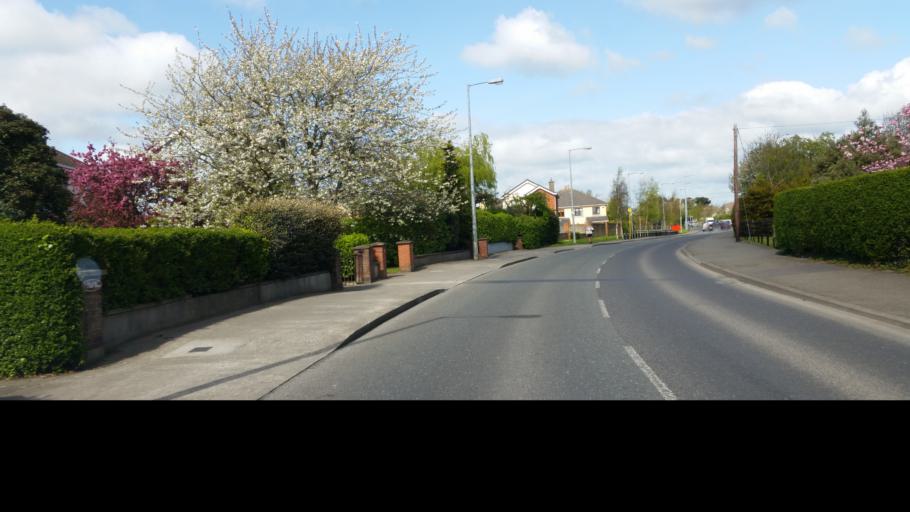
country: IE
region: Leinster
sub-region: Fingal County
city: Swords
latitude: 53.4656
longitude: -6.2368
